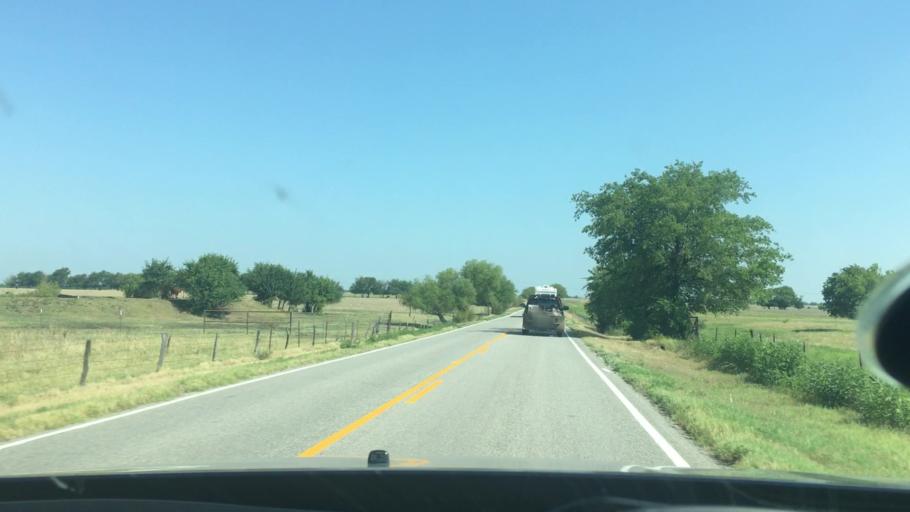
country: US
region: Oklahoma
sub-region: Johnston County
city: Tishomingo
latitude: 34.1537
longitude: -96.5062
